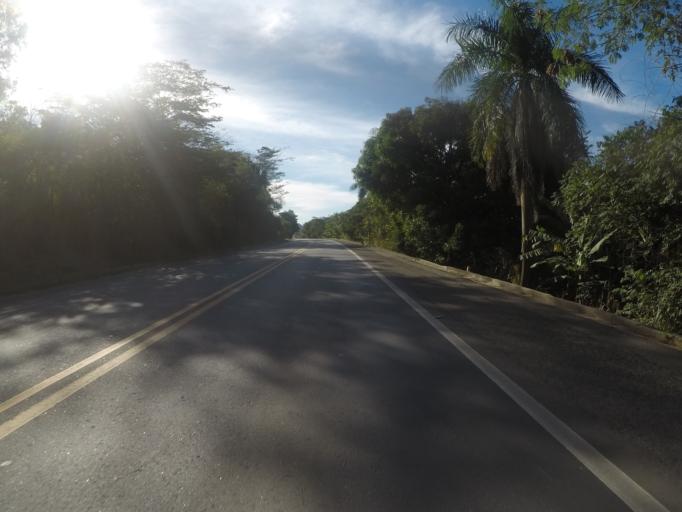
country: BR
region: Espirito Santo
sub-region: Fundao
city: Fundao
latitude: -19.9047
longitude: -40.4077
